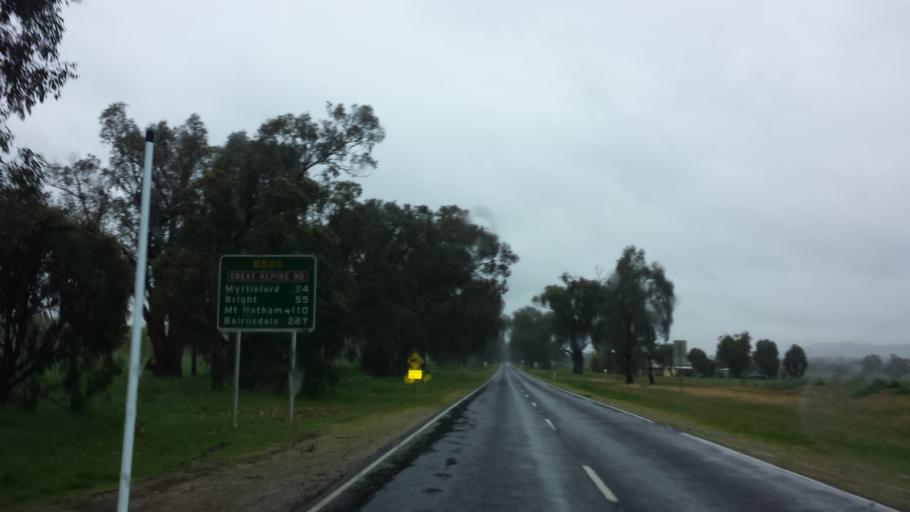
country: AU
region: Victoria
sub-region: Wangaratta
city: Wangaratta
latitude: -36.4371
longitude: 146.5451
